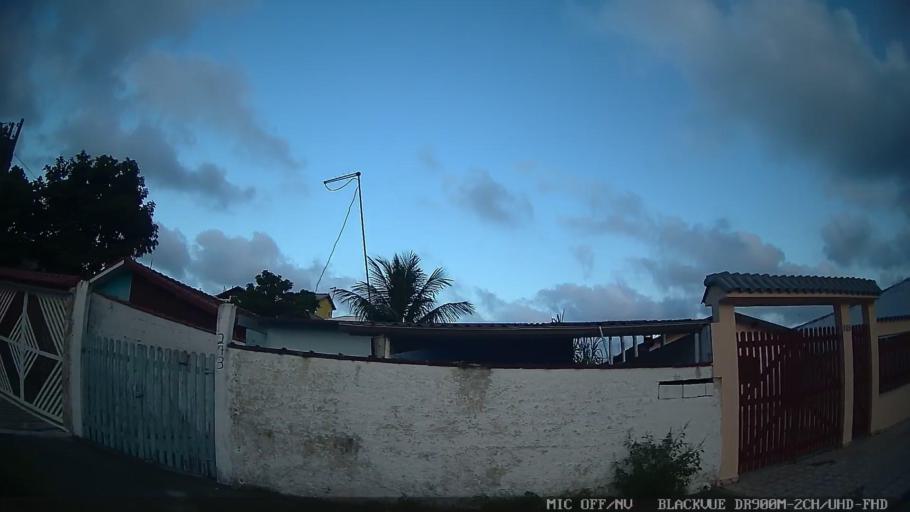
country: BR
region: Sao Paulo
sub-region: Peruibe
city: Peruibe
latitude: -24.3249
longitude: -47.0028
